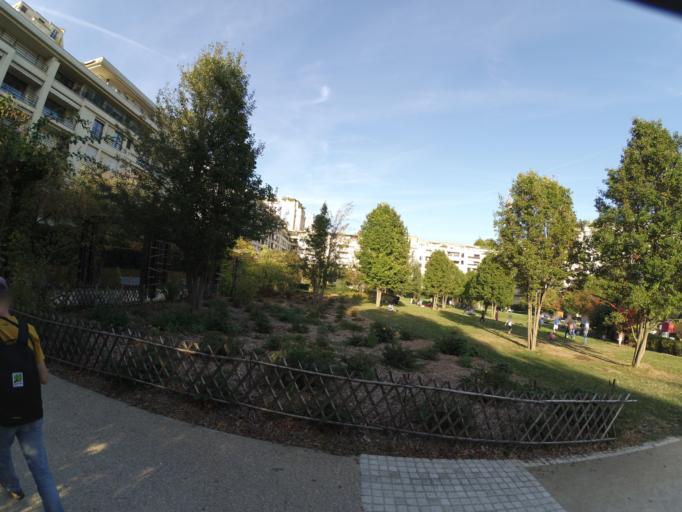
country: FR
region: Ile-de-France
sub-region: Departement des Hauts-de-Seine
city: Neuilly-sur-Seine
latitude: 48.8556
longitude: 2.2827
